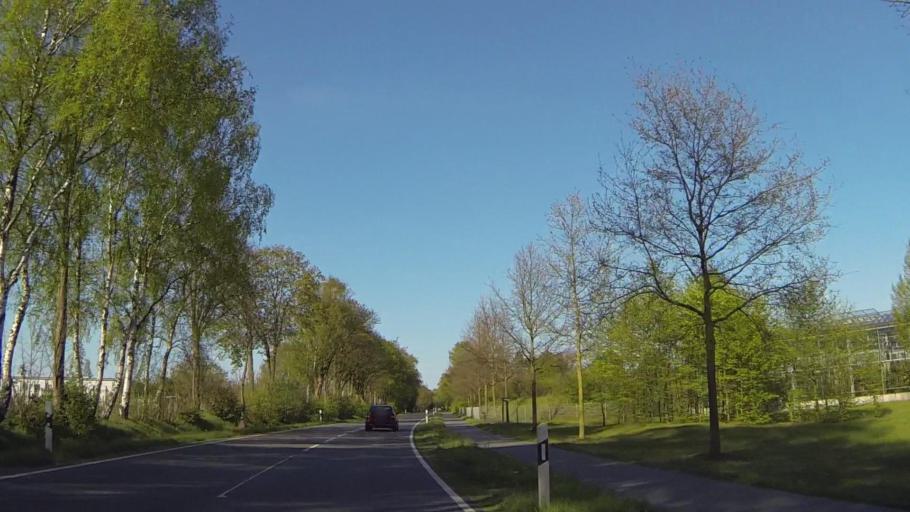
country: DE
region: Schleswig-Holstein
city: Appen
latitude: 53.6261
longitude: 9.7320
